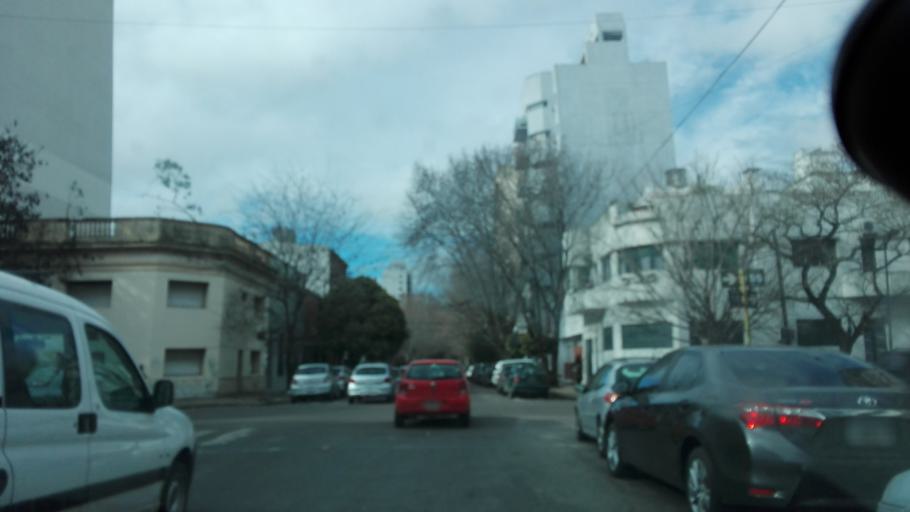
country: AR
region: Buenos Aires
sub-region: Partido de La Plata
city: La Plata
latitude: -34.9237
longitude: -57.9539
